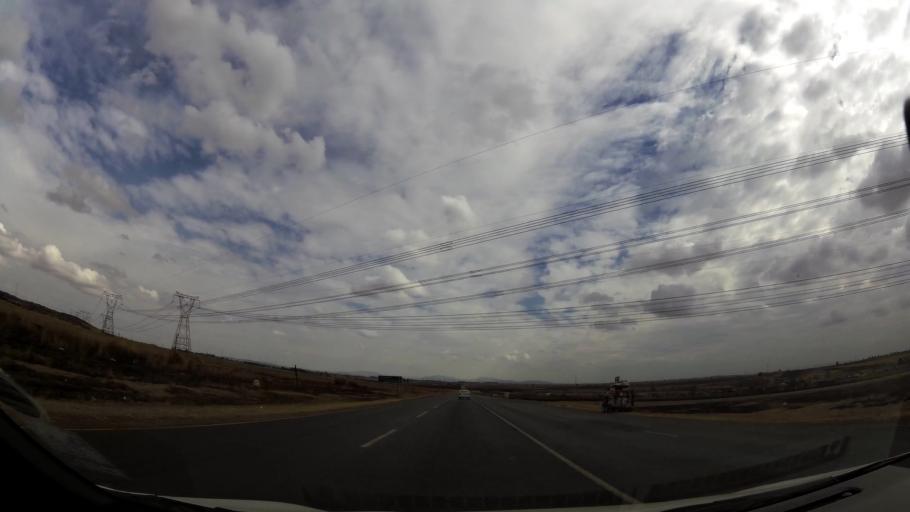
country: ZA
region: Gauteng
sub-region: Sedibeng District Municipality
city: Heidelberg
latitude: -26.4315
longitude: 28.1947
